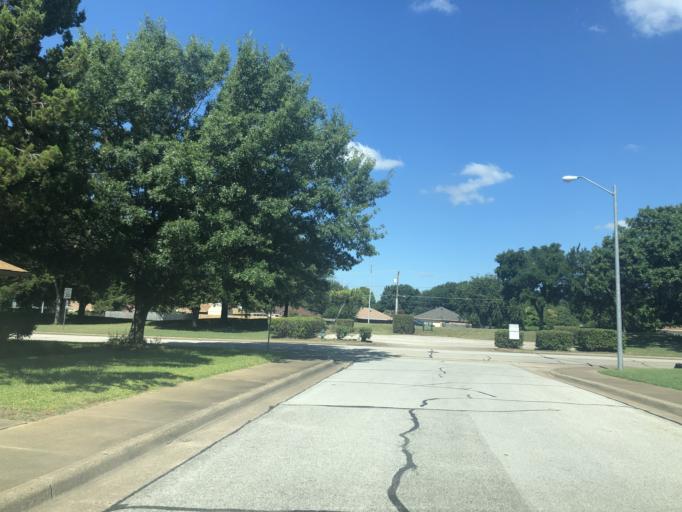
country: US
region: Texas
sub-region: Dallas County
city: Duncanville
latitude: 32.6443
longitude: -96.9403
